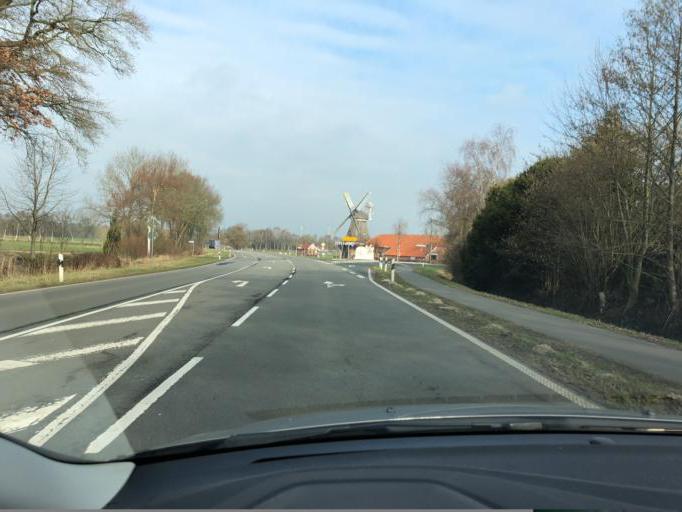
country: DE
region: Lower Saxony
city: Hesel
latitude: 53.3404
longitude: 7.6070
